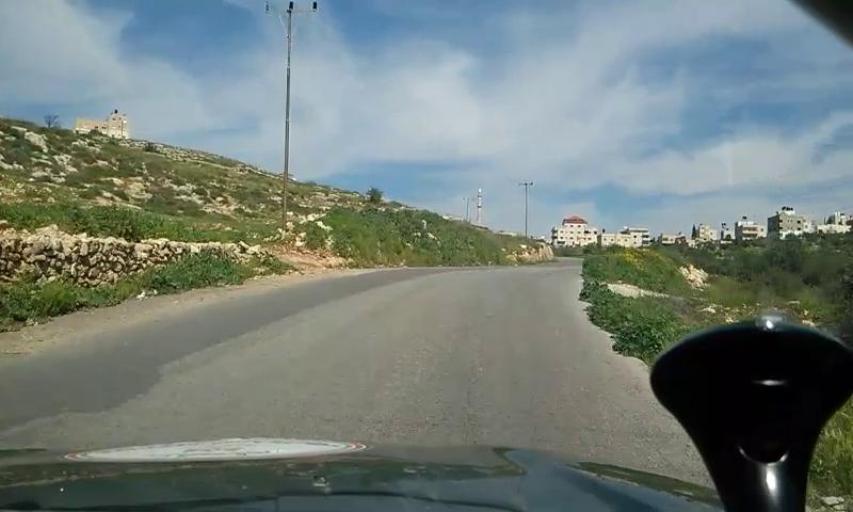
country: PS
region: West Bank
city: Bayt `Ur at Tahta
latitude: 31.8913
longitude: 35.0878
